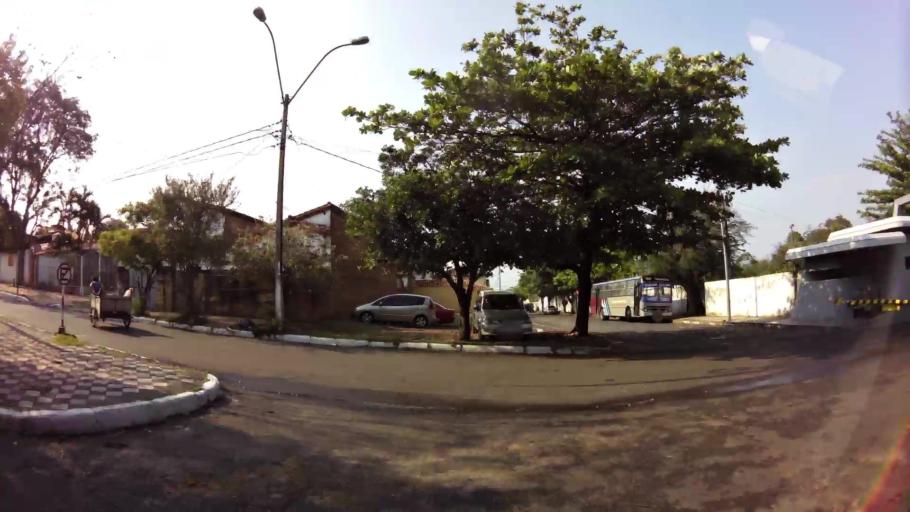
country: PY
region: Presidente Hayes
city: Nanawa
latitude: -25.2910
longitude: -57.6678
